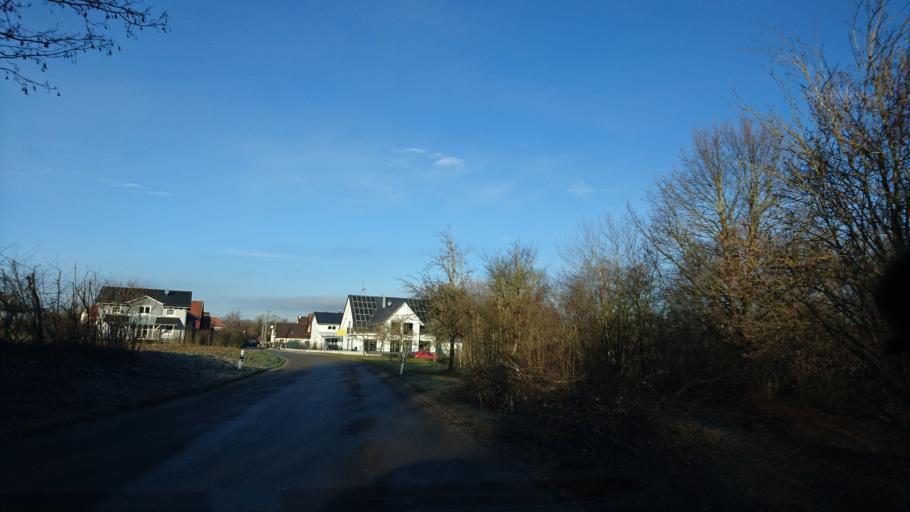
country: DE
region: Bavaria
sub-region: Swabia
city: Kuhlenthal
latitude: 48.5486
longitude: 10.7948
